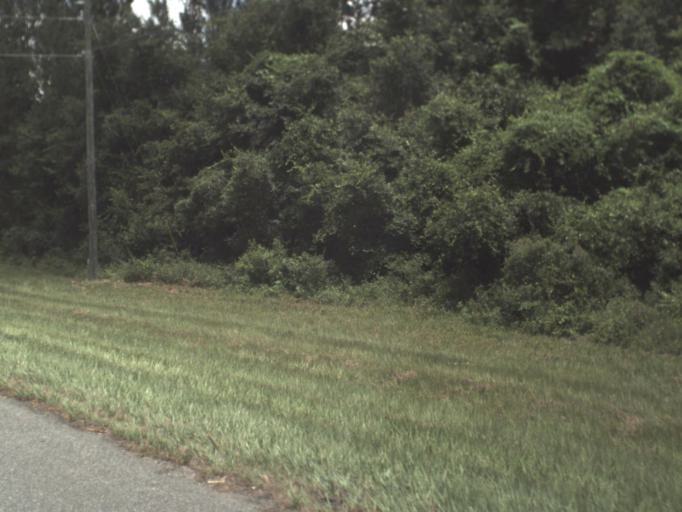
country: US
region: Florida
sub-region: Union County
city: Lake Butler
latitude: 30.0376
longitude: -82.3114
